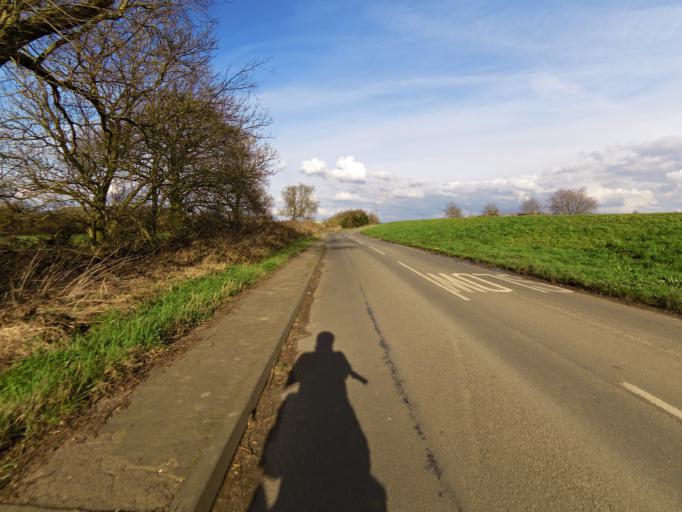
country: GB
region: England
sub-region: East Riding of Yorkshire
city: Snaith
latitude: 53.6915
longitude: -1.0429
